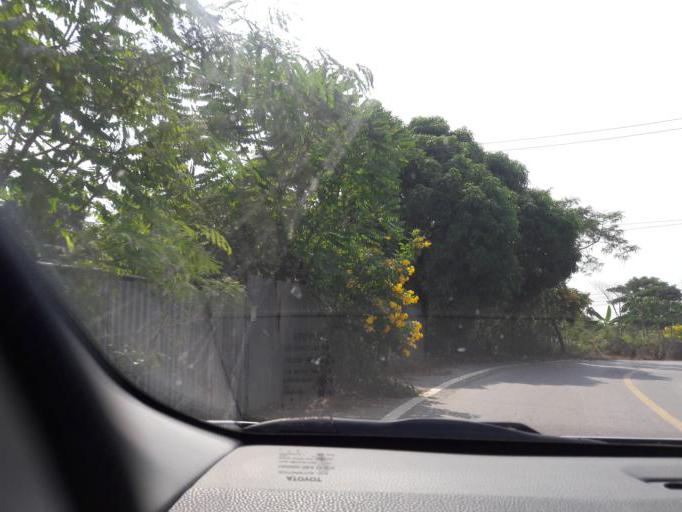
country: TH
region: Ang Thong
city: Ang Thong
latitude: 14.5703
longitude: 100.4251
